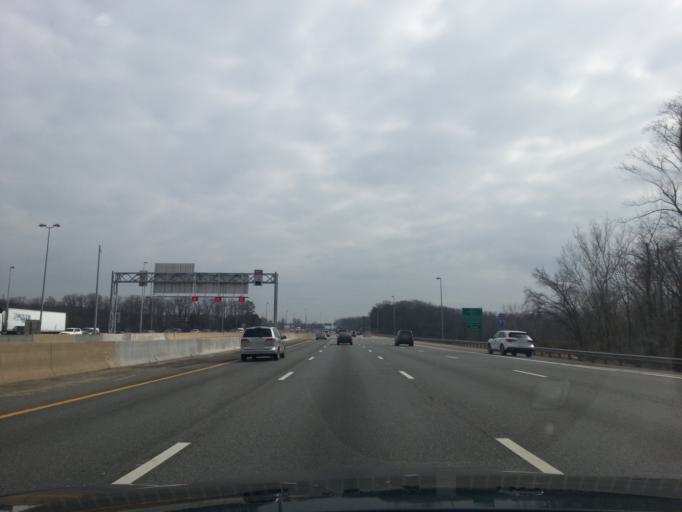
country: US
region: Virginia
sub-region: Prince William County
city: Woodbridge
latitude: 38.6713
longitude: -77.2484
